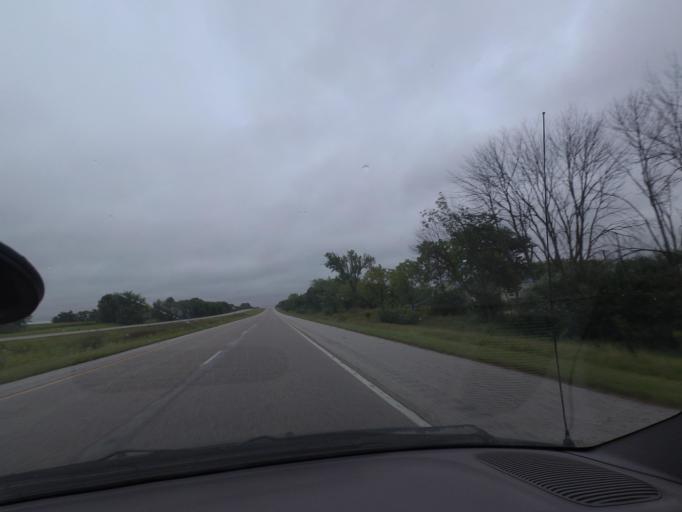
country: US
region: Illinois
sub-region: Scott County
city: Winchester
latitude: 39.6812
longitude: -90.4379
